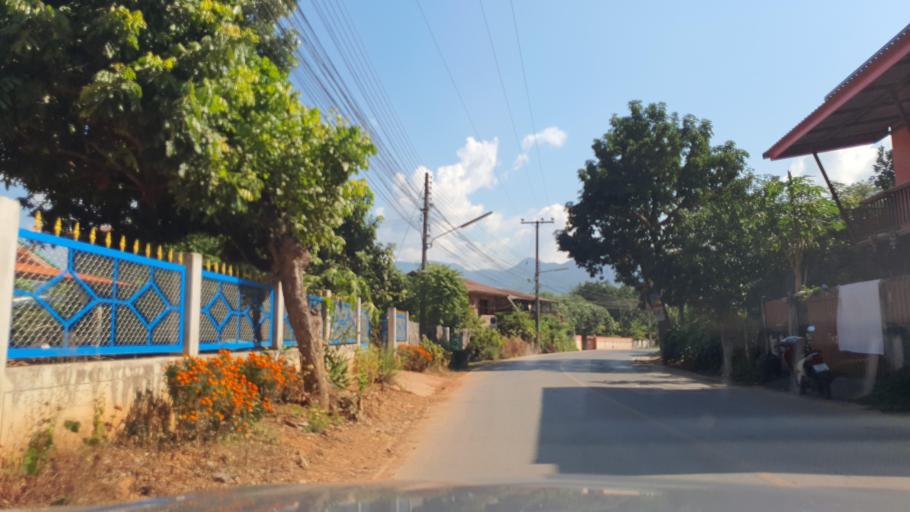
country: TH
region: Nan
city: Pua
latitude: 19.1407
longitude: 100.9320
